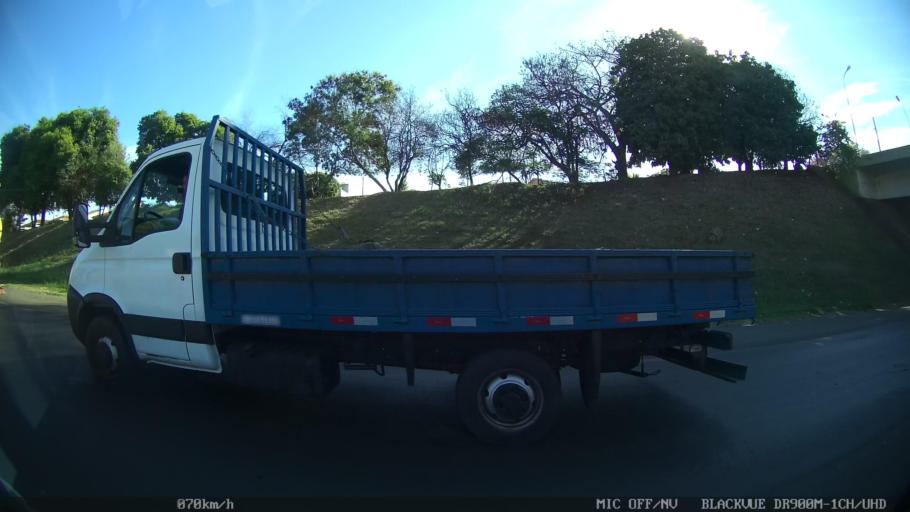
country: BR
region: Sao Paulo
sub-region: Sao Jose Do Rio Preto
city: Sao Jose do Rio Preto
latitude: -20.8126
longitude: -49.3568
